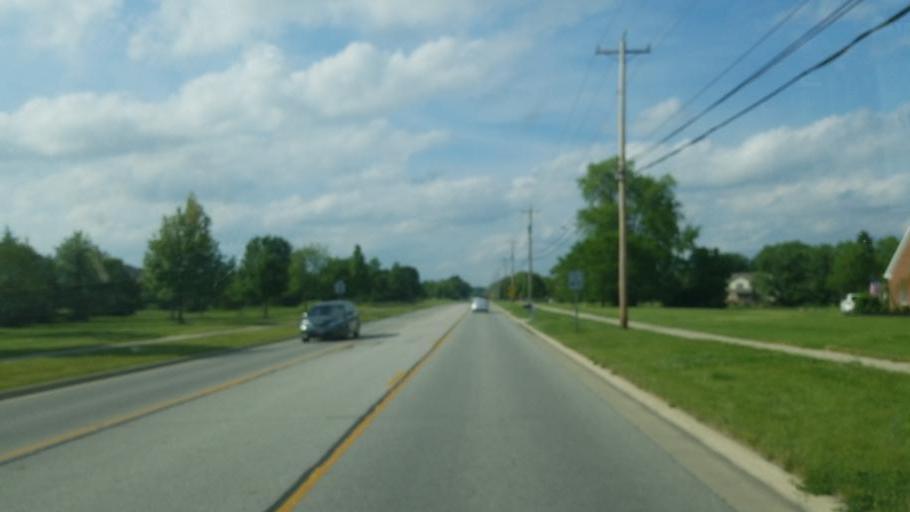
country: US
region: Ohio
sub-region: Franklin County
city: Westerville
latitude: 40.1574
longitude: -82.9004
